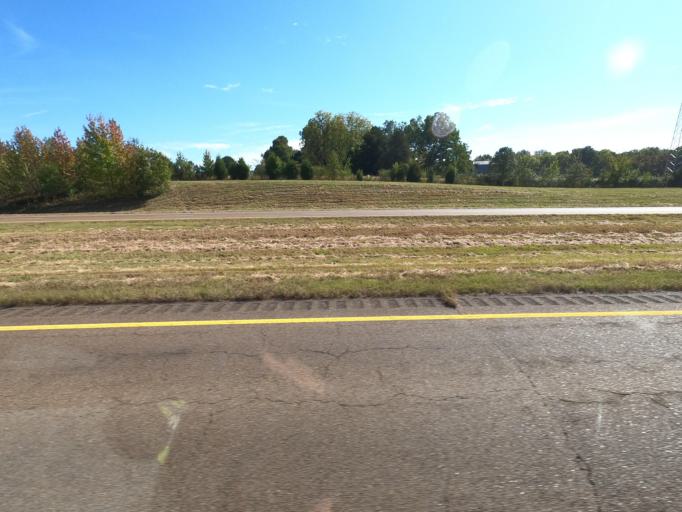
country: US
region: Tennessee
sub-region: Obion County
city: South Fulton
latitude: 36.4762
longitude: -88.9575
